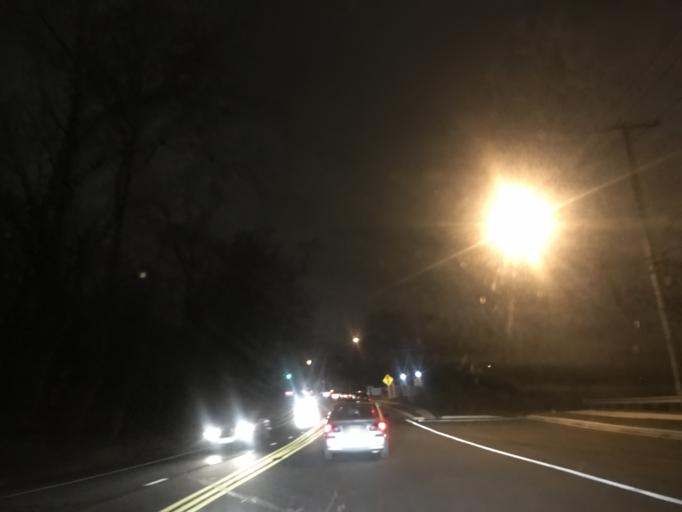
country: US
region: Maryland
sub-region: Prince George's County
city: Temple Hills
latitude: 38.8057
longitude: -76.9616
